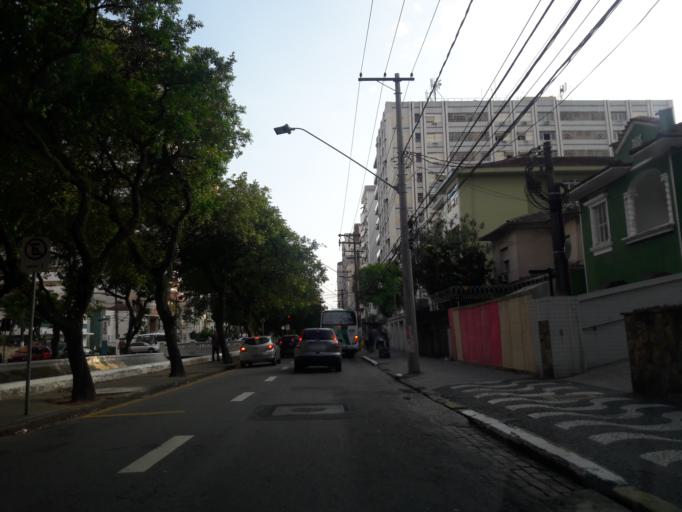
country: BR
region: Sao Paulo
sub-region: Santos
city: Santos
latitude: -23.9648
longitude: -46.3388
